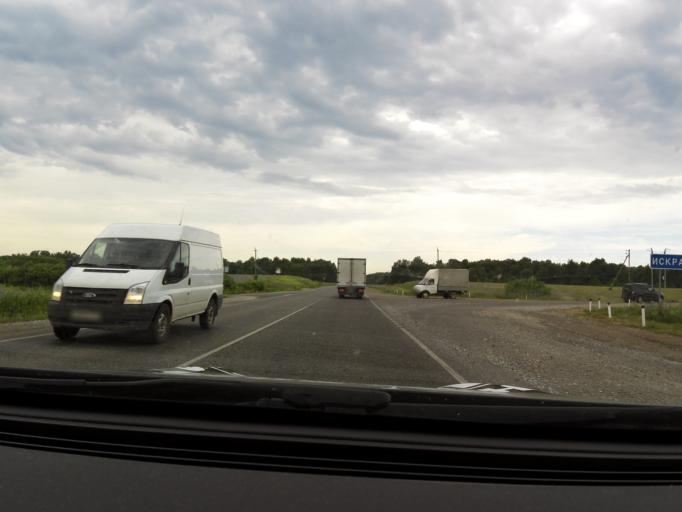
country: RU
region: Bashkortostan
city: Kudeyevskiy
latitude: 54.8139
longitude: 56.6837
